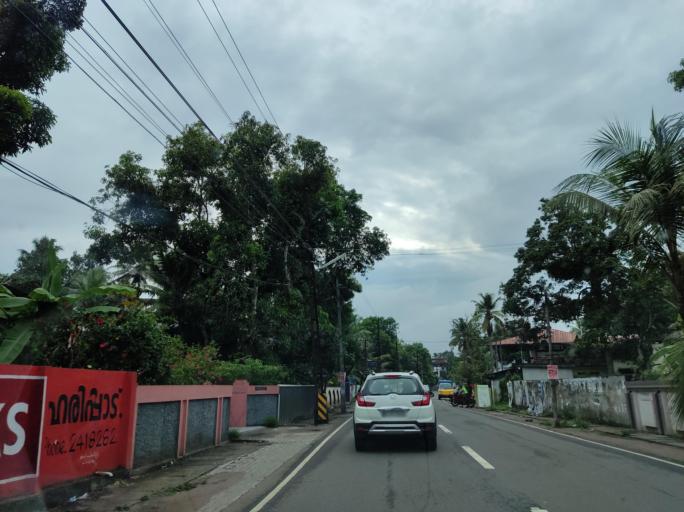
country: IN
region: Kerala
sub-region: Alappuzha
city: Mavelikara
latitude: 9.2513
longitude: 76.4990
